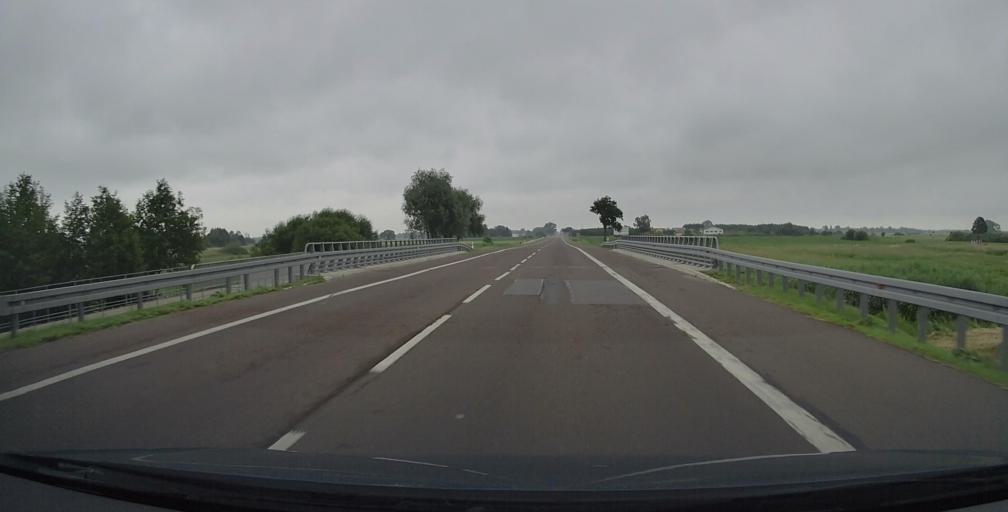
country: PL
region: Lublin Voivodeship
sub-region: Powiat bialski
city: Terespol
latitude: 52.0573
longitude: 23.5708
